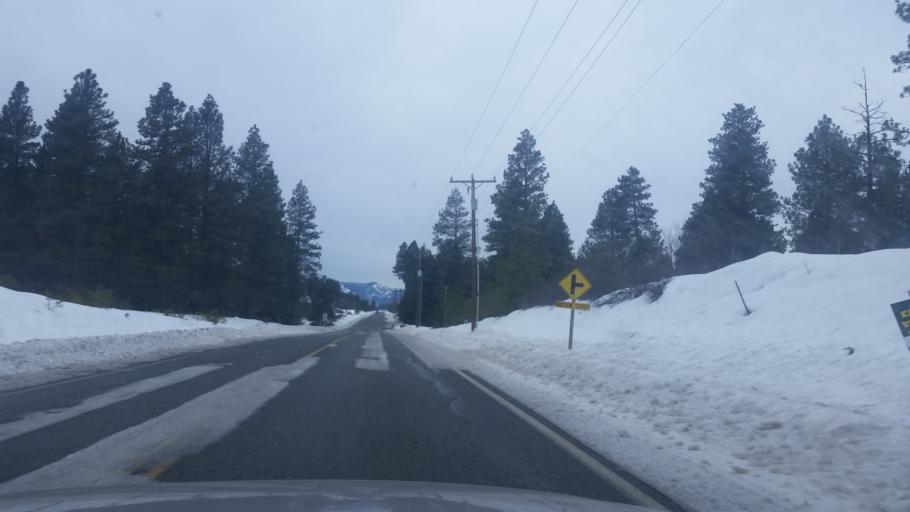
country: US
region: Washington
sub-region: Kittitas County
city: Cle Elum
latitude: 47.1604
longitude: -120.8874
